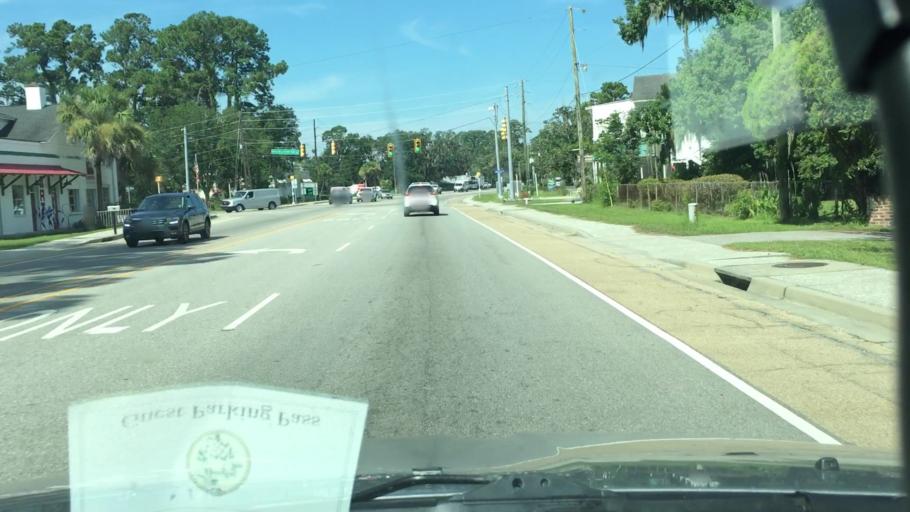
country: US
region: South Carolina
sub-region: Beaufort County
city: Beaufort
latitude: 32.3973
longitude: -80.5756
